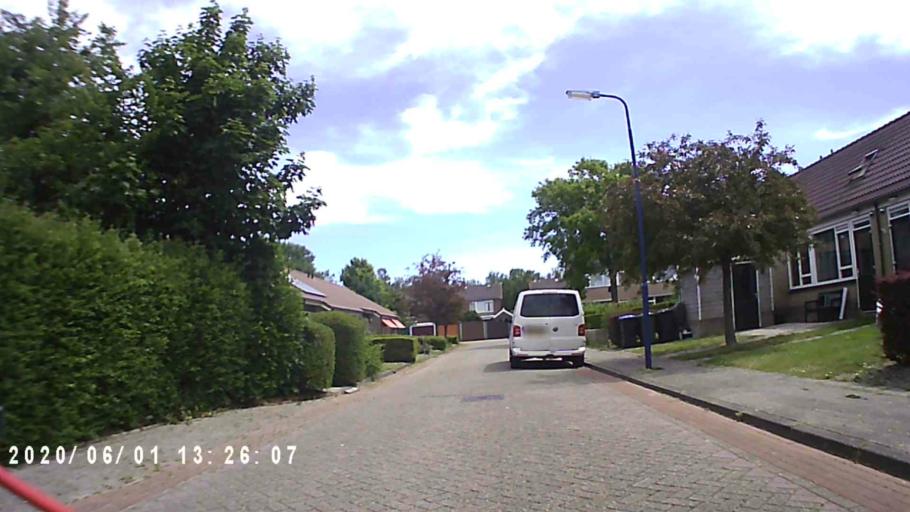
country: NL
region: Friesland
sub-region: Gemeente Littenseradiel
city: Wommels
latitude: 53.1059
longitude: 5.5819
